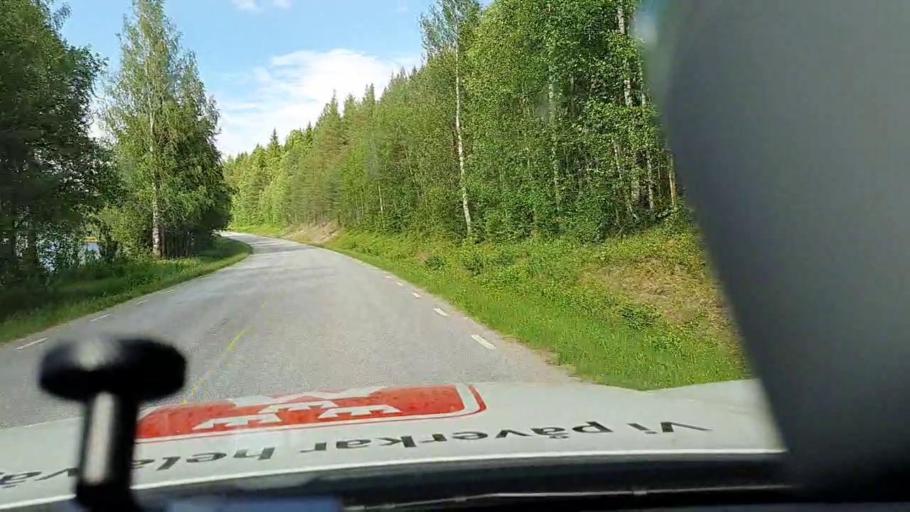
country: SE
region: Norrbotten
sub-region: Gallivare Kommun
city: Gaellivare
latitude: 66.4454
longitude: 20.6513
